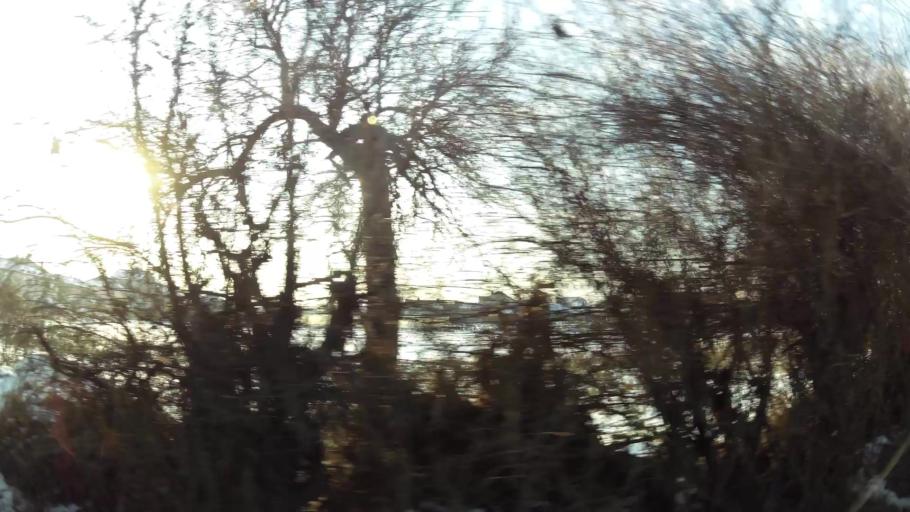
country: MK
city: Creshevo
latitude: 42.0270
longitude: 21.5200
